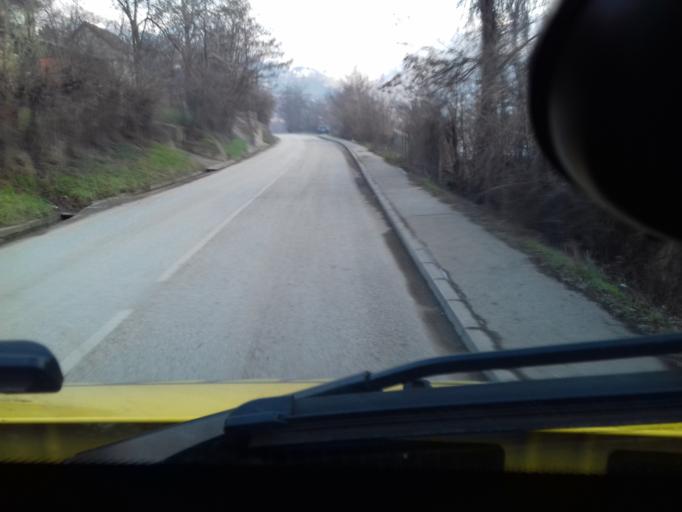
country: BA
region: Federation of Bosnia and Herzegovina
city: Zenica
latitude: 44.2324
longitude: 17.8890
